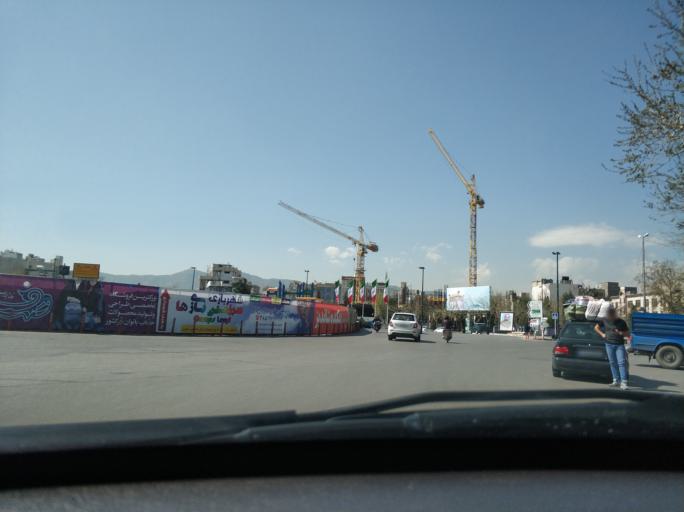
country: IR
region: Razavi Khorasan
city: Mashhad
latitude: 36.2687
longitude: 59.5990
